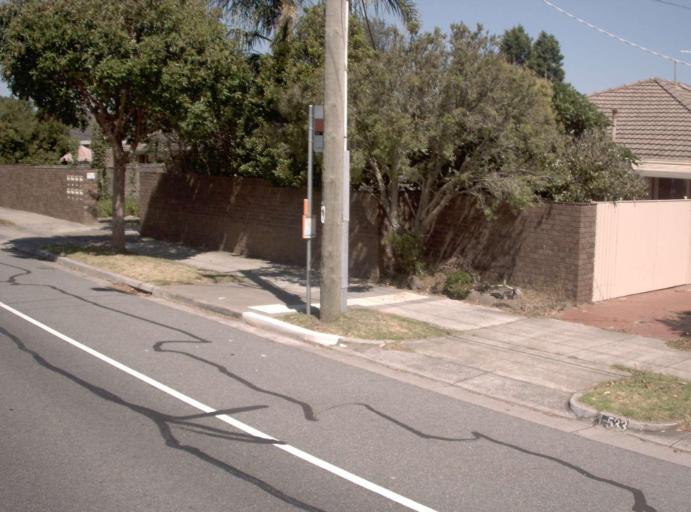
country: AU
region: Victoria
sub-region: Bayside
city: Black Rock
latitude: -37.9764
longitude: 145.0239
